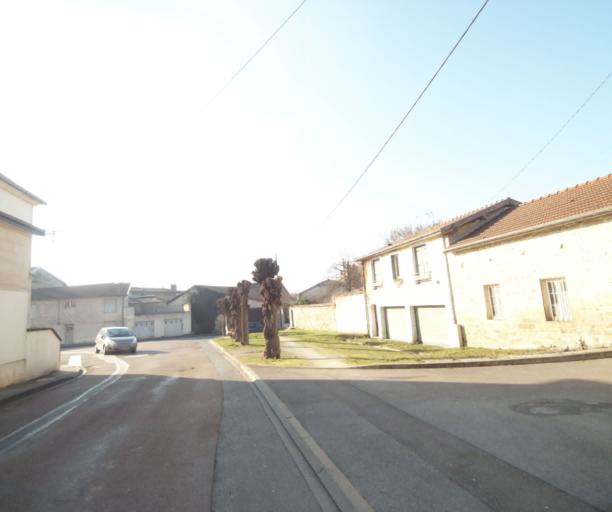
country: FR
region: Champagne-Ardenne
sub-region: Departement de la Haute-Marne
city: Wassy
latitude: 48.4991
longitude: 4.9503
